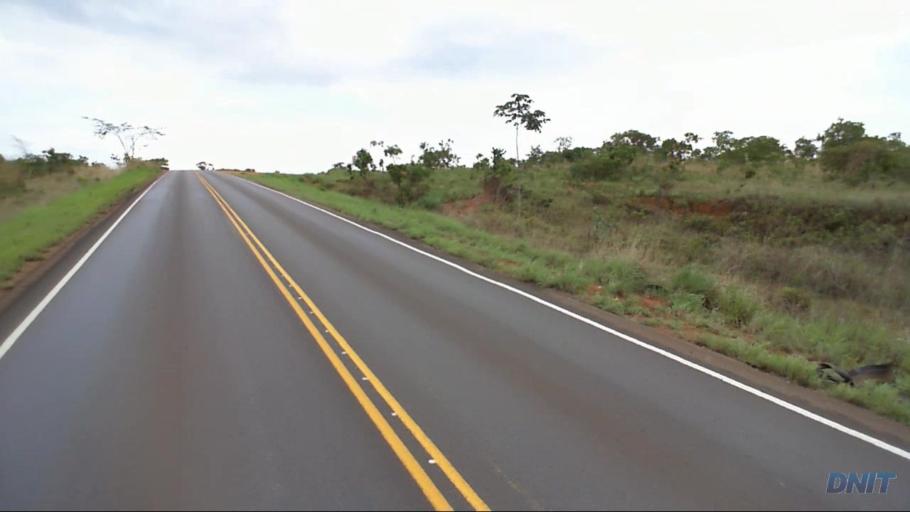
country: BR
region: Goias
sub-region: Padre Bernardo
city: Padre Bernardo
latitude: -15.2945
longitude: -48.2407
